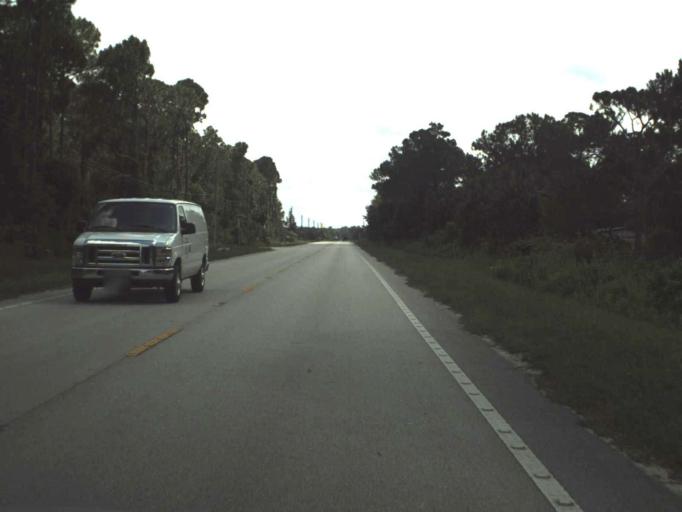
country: US
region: Florida
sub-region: Volusia County
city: Samsula-Spruce Creek
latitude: 28.9717
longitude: -81.0823
